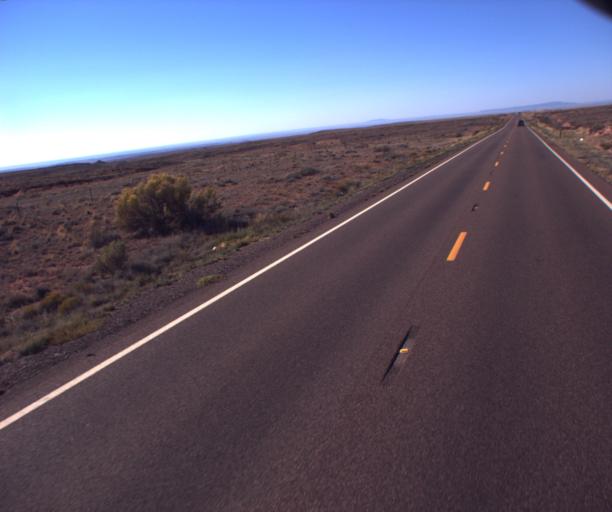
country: US
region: Arizona
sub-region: Navajo County
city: Winslow
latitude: 35.1354
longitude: -110.4906
